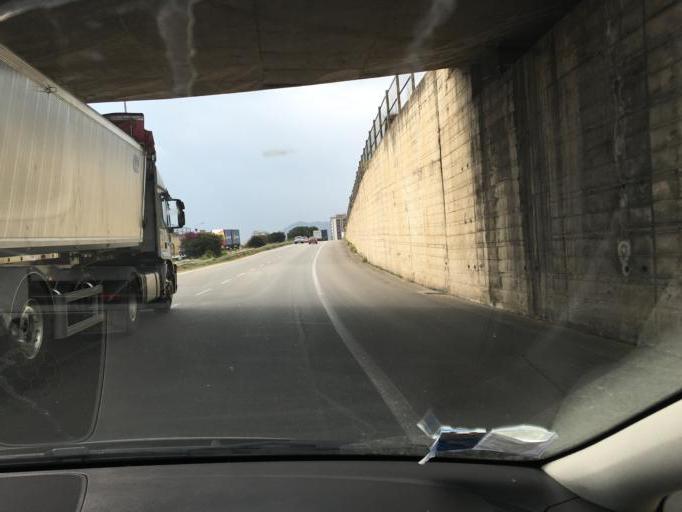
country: IT
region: Sicily
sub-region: Palermo
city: Palermo
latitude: 38.1486
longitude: 13.3265
